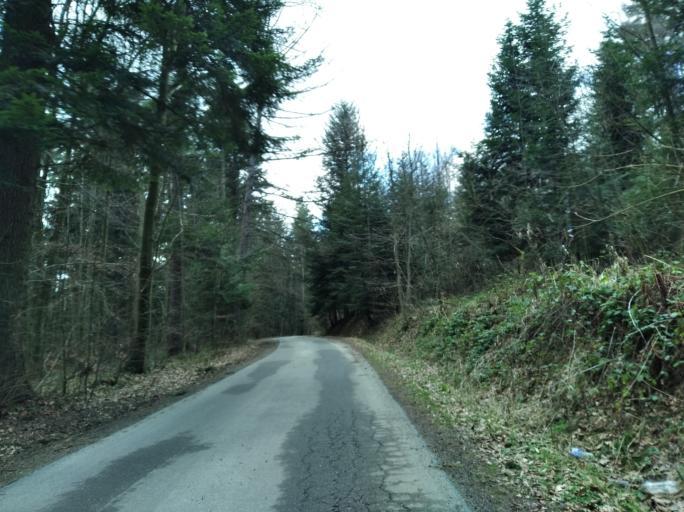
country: PL
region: Subcarpathian Voivodeship
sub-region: Powiat strzyzowski
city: Wysoka Strzyzowska
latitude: 49.7993
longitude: 21.7349
